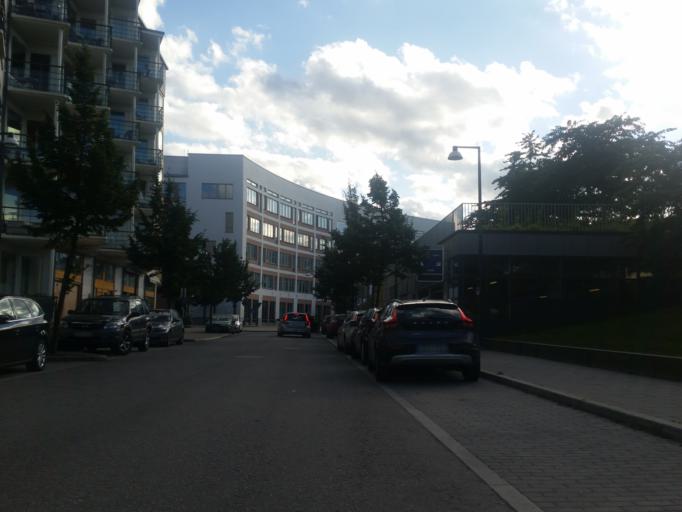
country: SE
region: Stockholm
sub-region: Stockholms Kommun
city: OEstermalm
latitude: 59.3047
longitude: 18.0981
